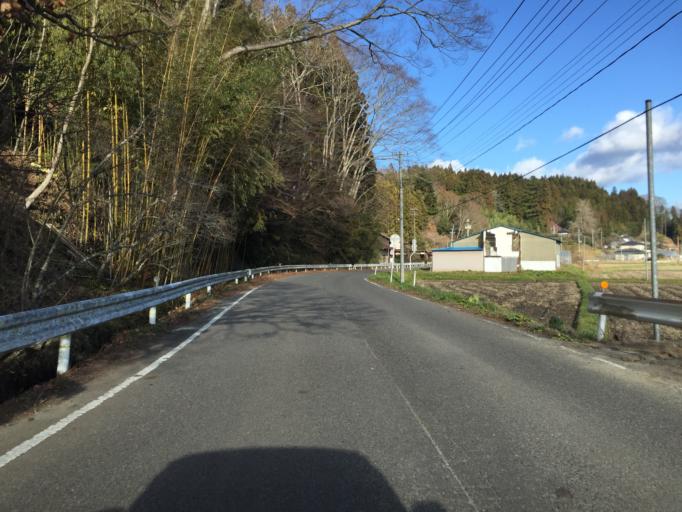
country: JP
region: Fukushima
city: Ishikawa
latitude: 37.2281
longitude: 140.6065
